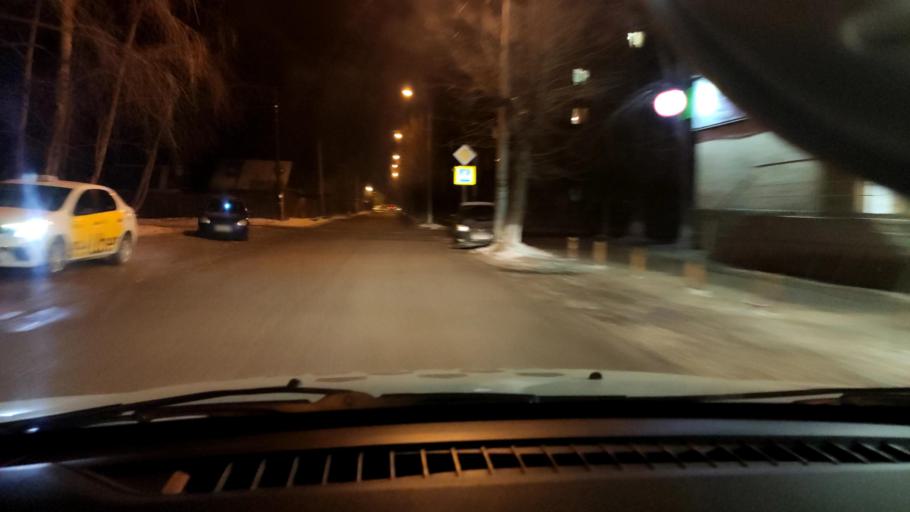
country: RU
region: Perm
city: Overyata
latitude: 58.0287
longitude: 55.8418
